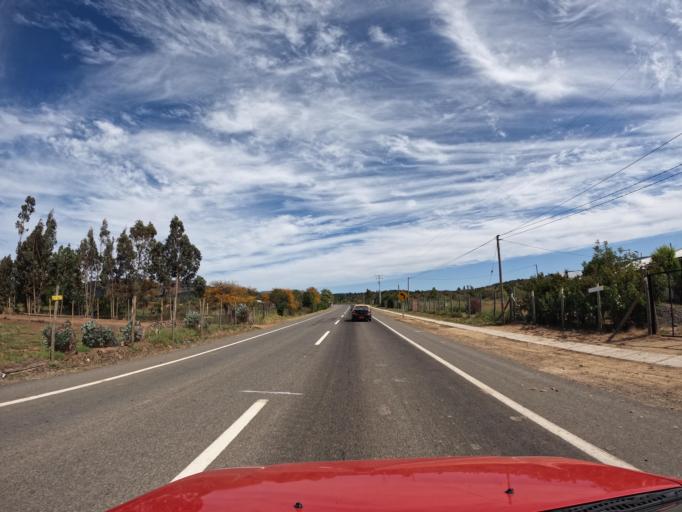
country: CL
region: Maule
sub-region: Provincia de Talca
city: Talca
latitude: -35.1238
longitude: -71.9578
